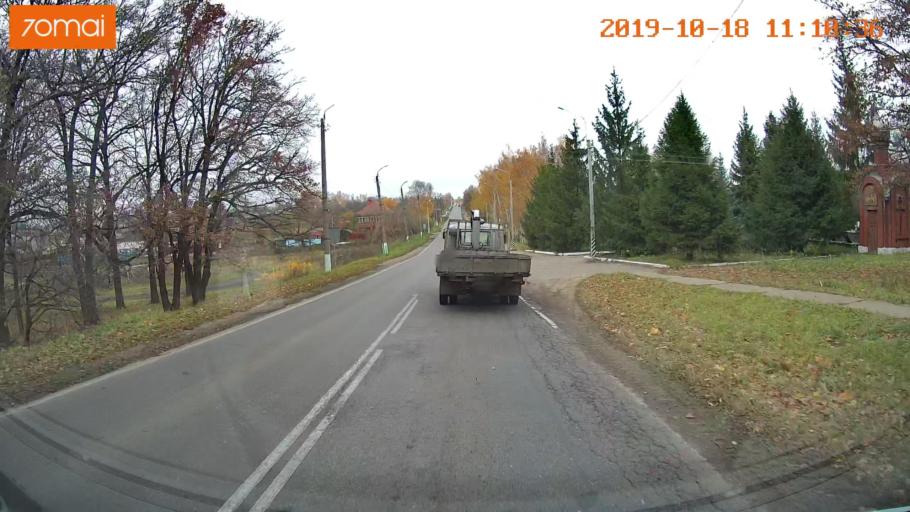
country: RU
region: Tula
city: Kimovsk
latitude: 53.9567
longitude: 38.5386
